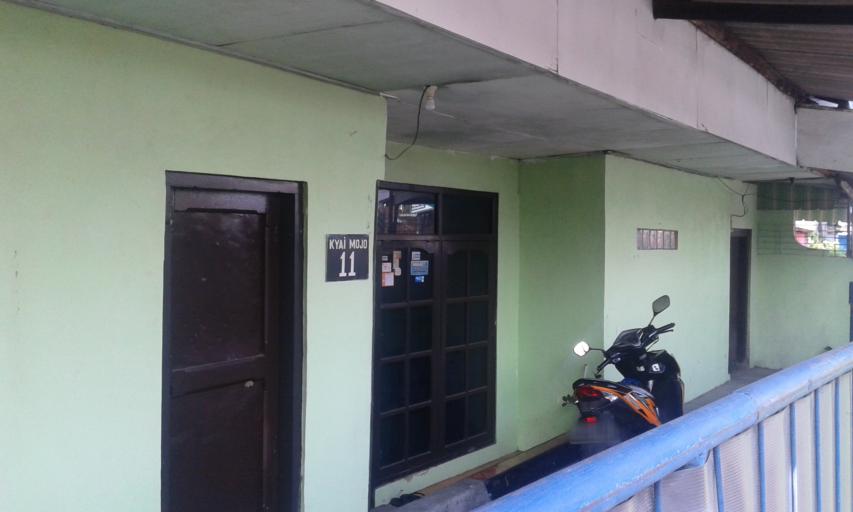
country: ID
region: Daerah Istimewa Yogyakarta
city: Yogyakarta
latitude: -7.7828
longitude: 110.3583
